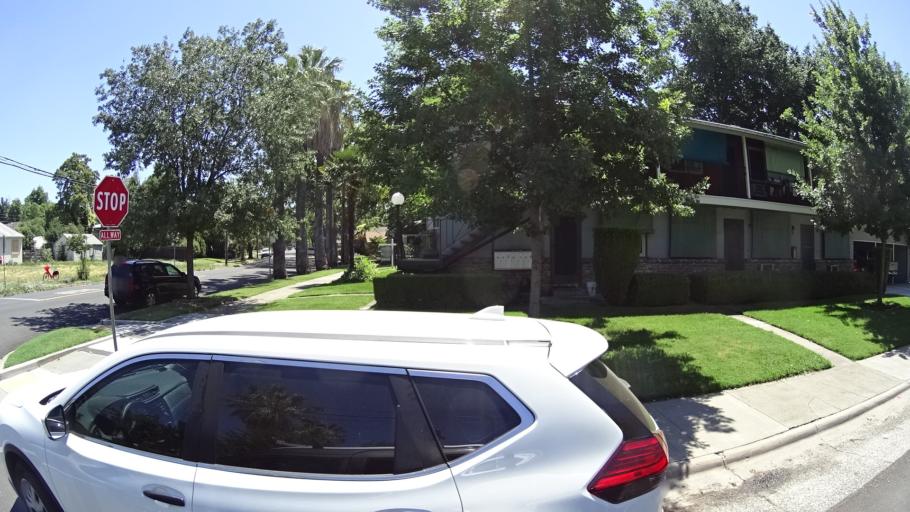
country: US
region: California
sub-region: Sacramento County
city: Sacramento
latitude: 38.5543
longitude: -121.4806
